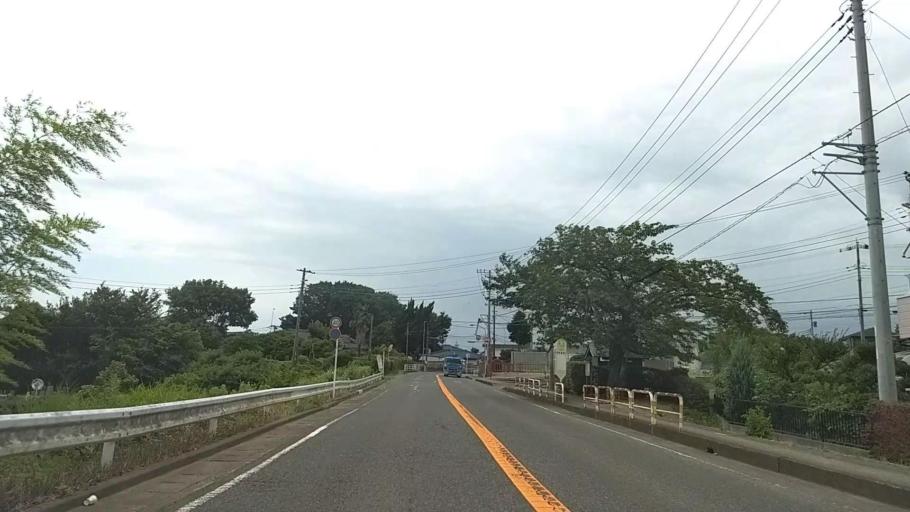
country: JP
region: Kanagawa
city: Chigasaki
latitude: 35.3672
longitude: 139.4061
